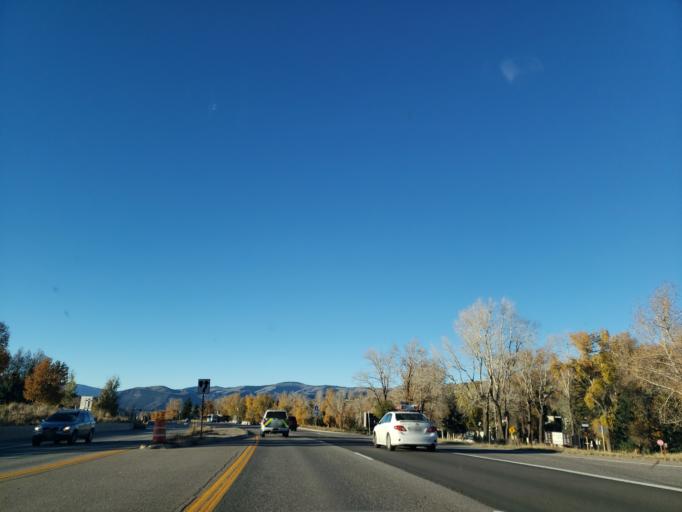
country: US
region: Colorado
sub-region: Pitkin County
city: Aspen
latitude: 39.2176
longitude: -106.8615
